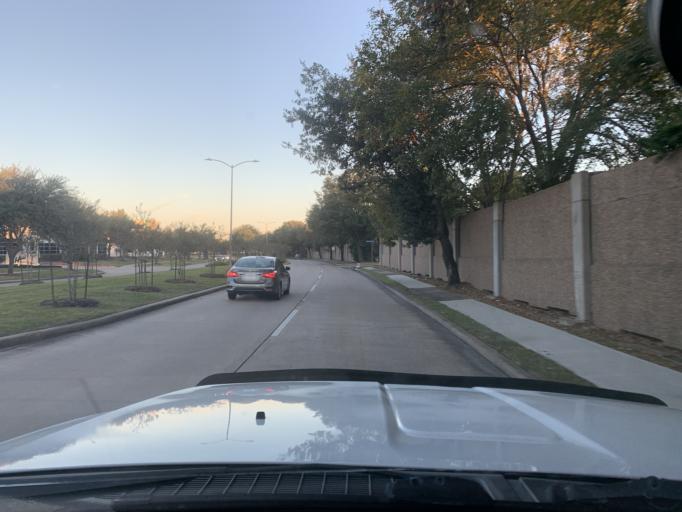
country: US
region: Texas
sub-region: Fort Bend County
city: Meadows Place
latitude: 29.6487
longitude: -95.6136
